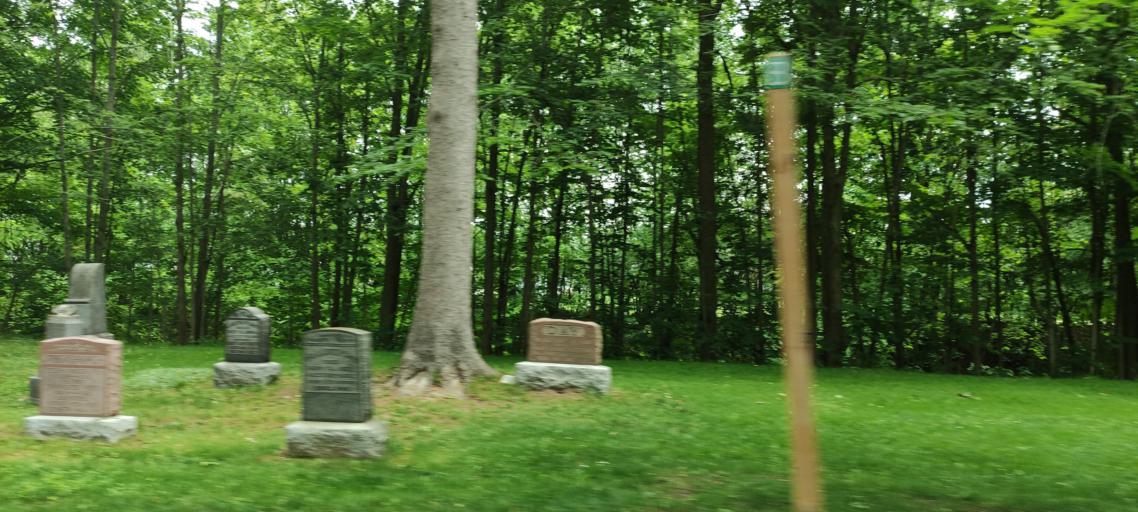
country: CA
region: Ontario
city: Stratford
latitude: 43.3726
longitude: -80.9980
